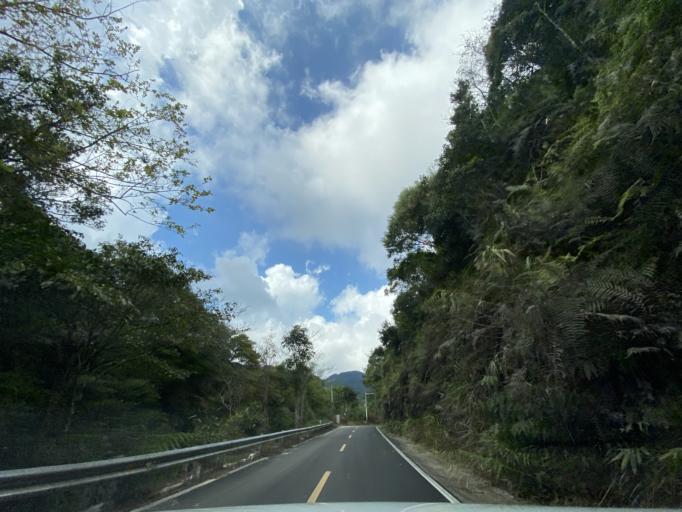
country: CN
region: Hainan
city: Diaoluoshan
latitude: 18.7223
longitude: 109.8698
